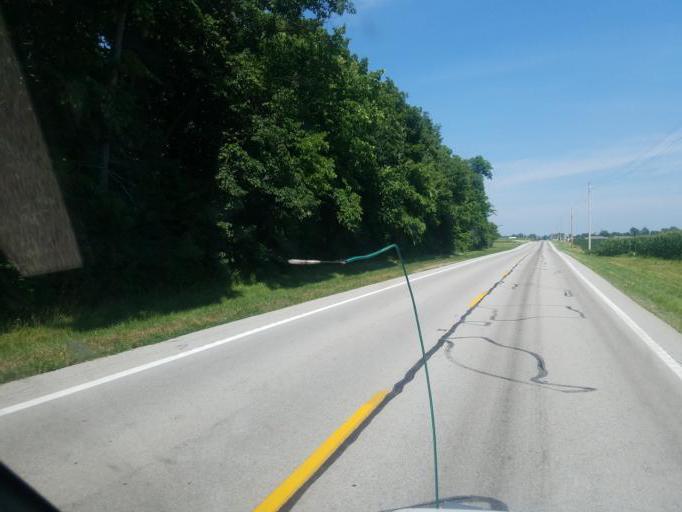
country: US
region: Ohio
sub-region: Auglaize County
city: Saint Marys
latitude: 40.4957
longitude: -84.3356
